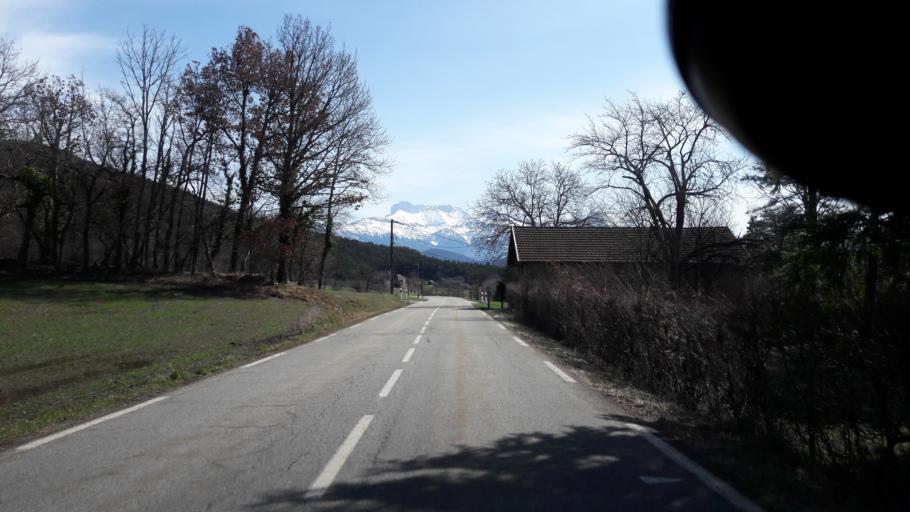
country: FR
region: Rhone-Alpes
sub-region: Departement de l'Isere
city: La Motte-Saint-Martin
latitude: 44.8857
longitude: 5.6417
